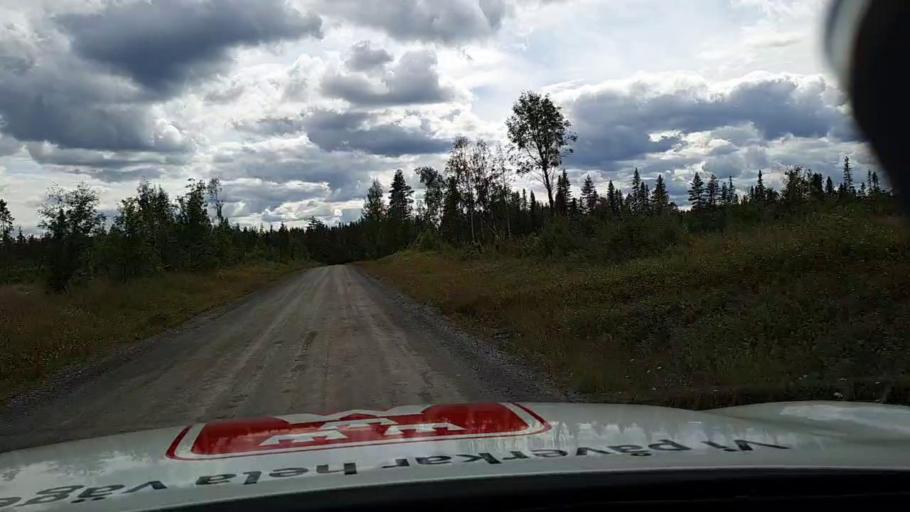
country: SE
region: Jaemtland
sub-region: Braecke Kommun
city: Braecke
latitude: 63.2658
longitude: 15.3782
